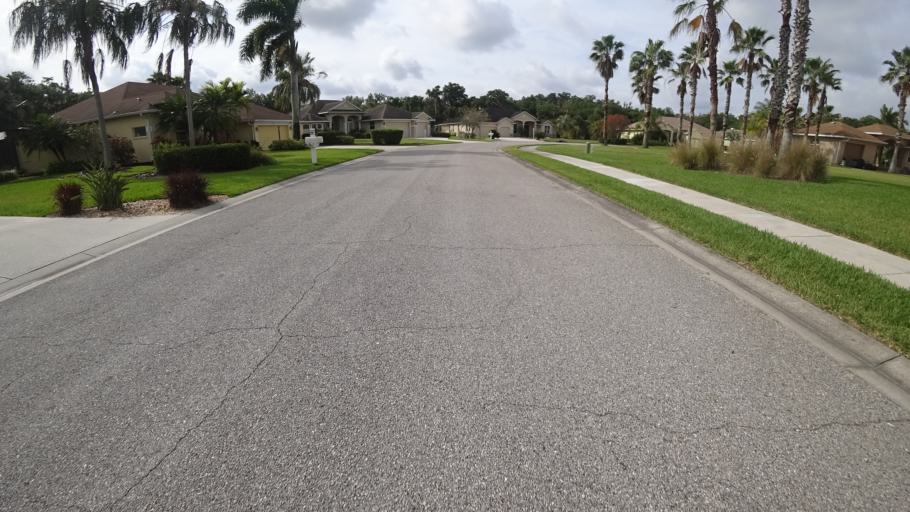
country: US
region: Florida
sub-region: Manatee County
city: Ellenton
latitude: 27.5625
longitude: -82.4676
